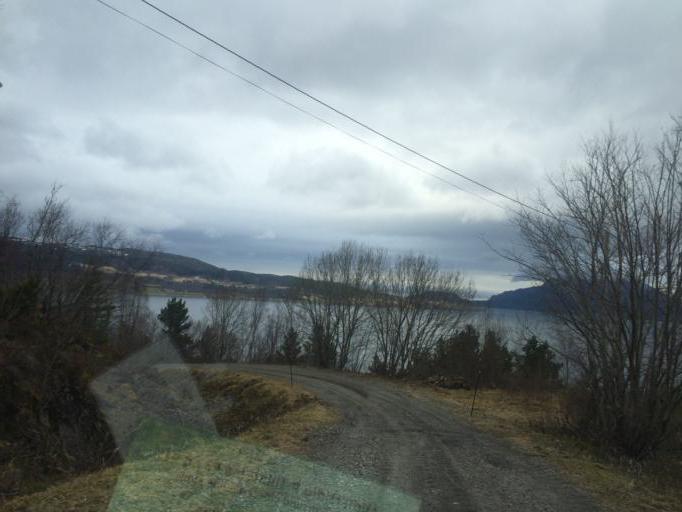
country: NO
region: More og Romsdal
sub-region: Gjemnes
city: Batnfjordsora
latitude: 62.9649
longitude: 7.7328
